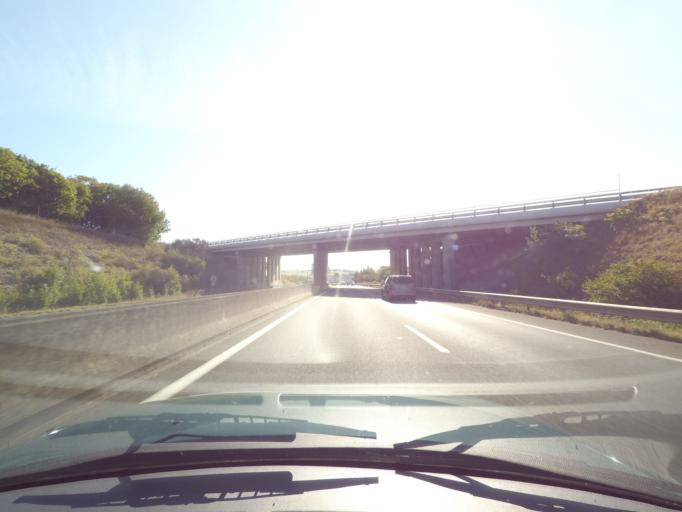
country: FR
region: Poitou-Charentes
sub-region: Departement de la Vienne
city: Migne-Auxances
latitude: 46.6198
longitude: 0.3439
